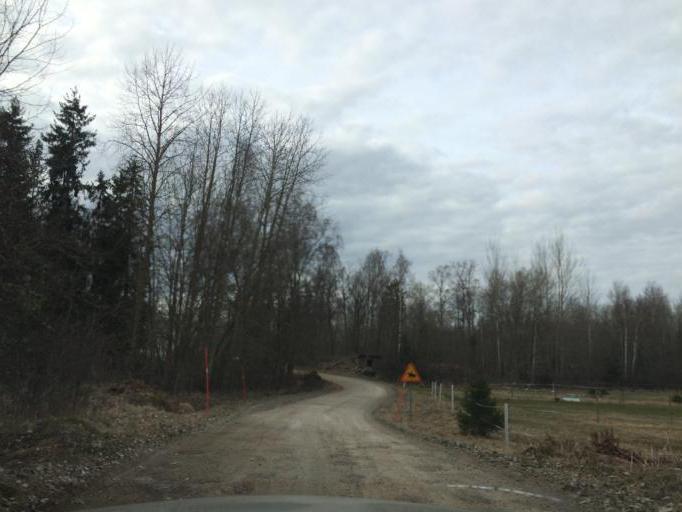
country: SE
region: Soedermanland
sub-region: Eskilstuna Kommun
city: Hallbybrunn
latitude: 59.4135
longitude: 16.4048
